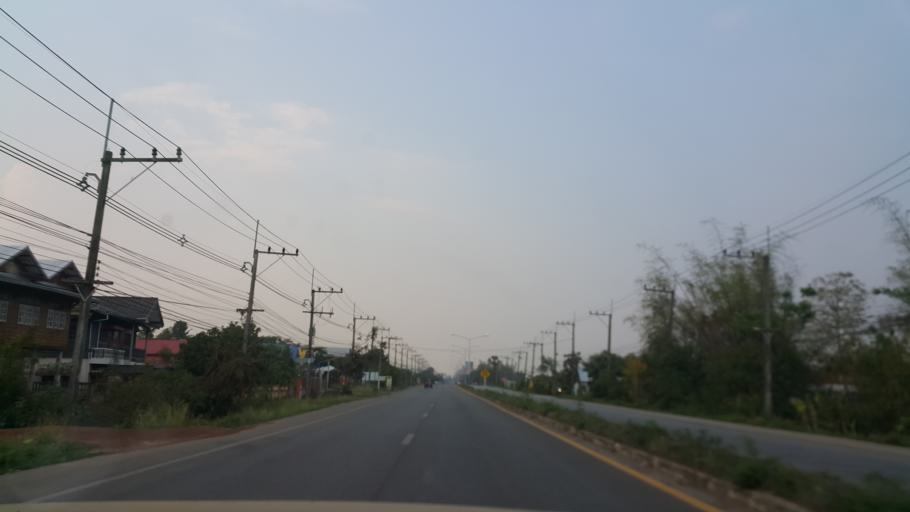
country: TH
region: Nakhon Phanom
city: That Phanom
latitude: 16.9948
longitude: 104.7237
